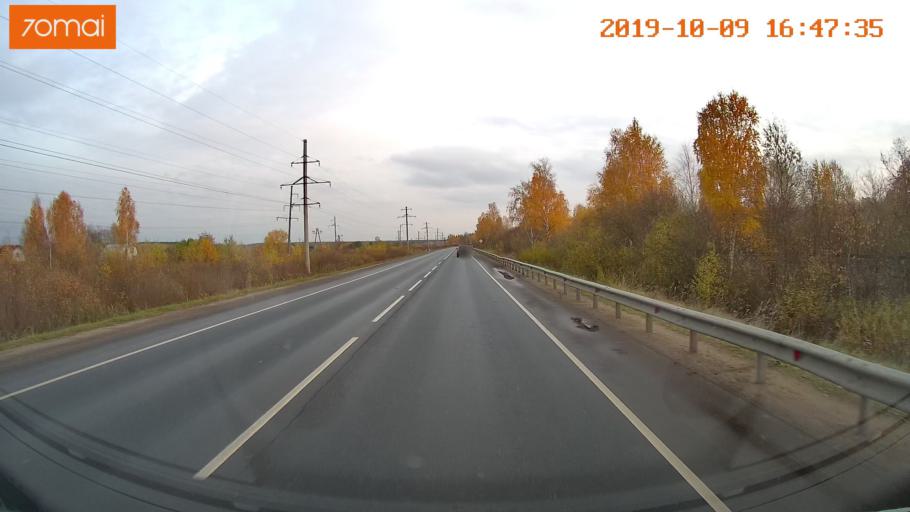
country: RU
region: Kostroma
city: Volgorechensk
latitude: 57.4360
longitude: 41.1794
